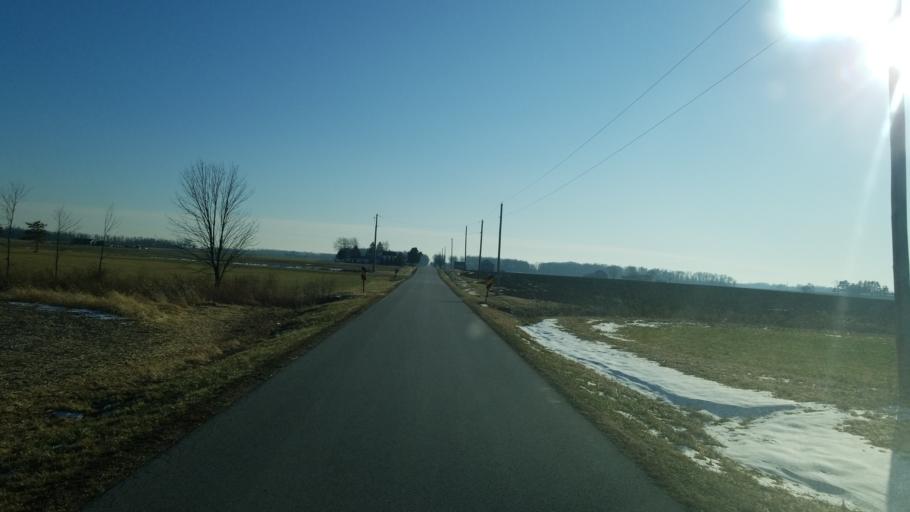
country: US
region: Ohio
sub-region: Sandusky County
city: Green Springs
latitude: 41.2201
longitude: -82.9948
